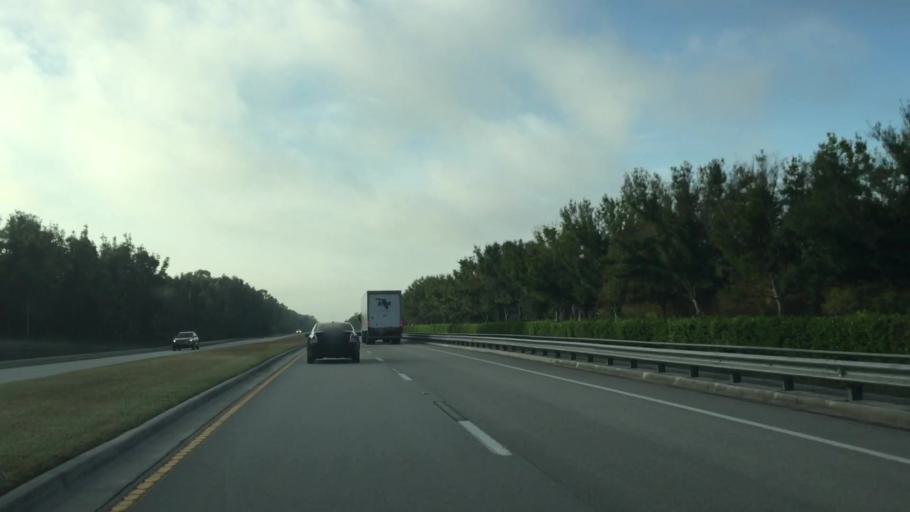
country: US
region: Florida
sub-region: Lee County
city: Estero
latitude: 26.4121
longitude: -81.8049
